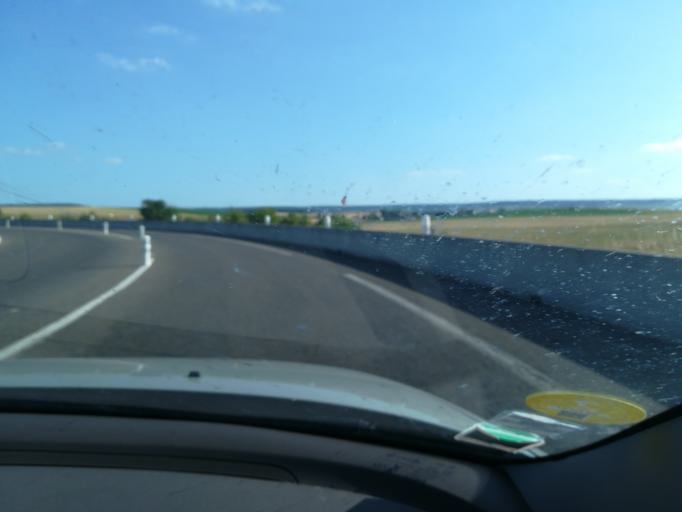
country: FR
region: Champagne-Ardenne
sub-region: Departement de la Marne
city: Bezannes
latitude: 49.2042
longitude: 4.0055
